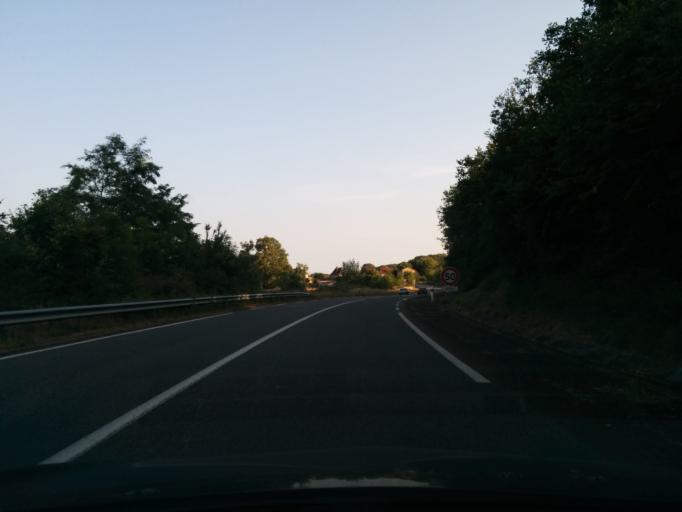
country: FR
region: Midi-Pyrenees
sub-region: Departement du Lot
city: Pradines
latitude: 44.5639
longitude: 1.4722
